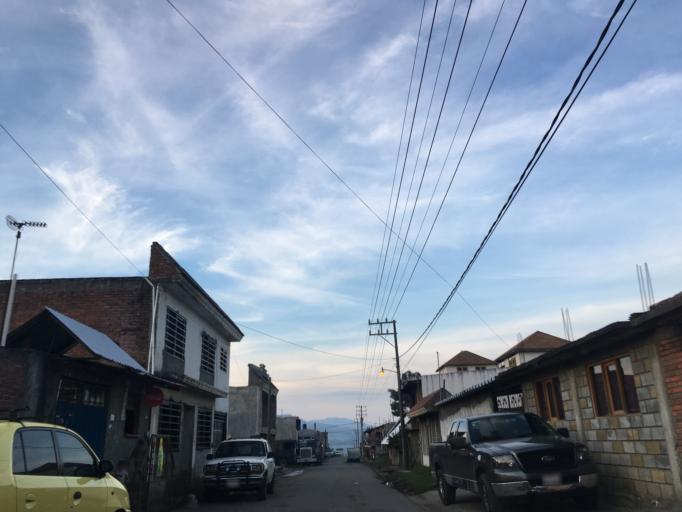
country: MX
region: Michoacan
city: Charapan
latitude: 19.6045
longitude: -102.2337
